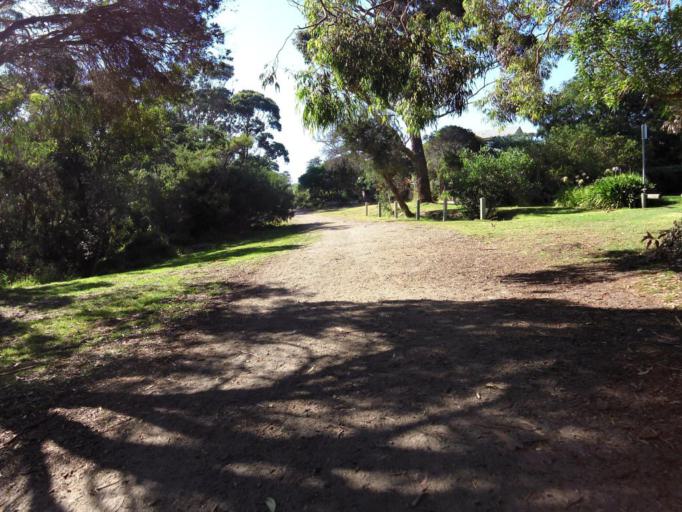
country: AU
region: Victoria
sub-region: Mornington Peninsula
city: Mount Martha
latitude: -38.2659
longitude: 145.0172
